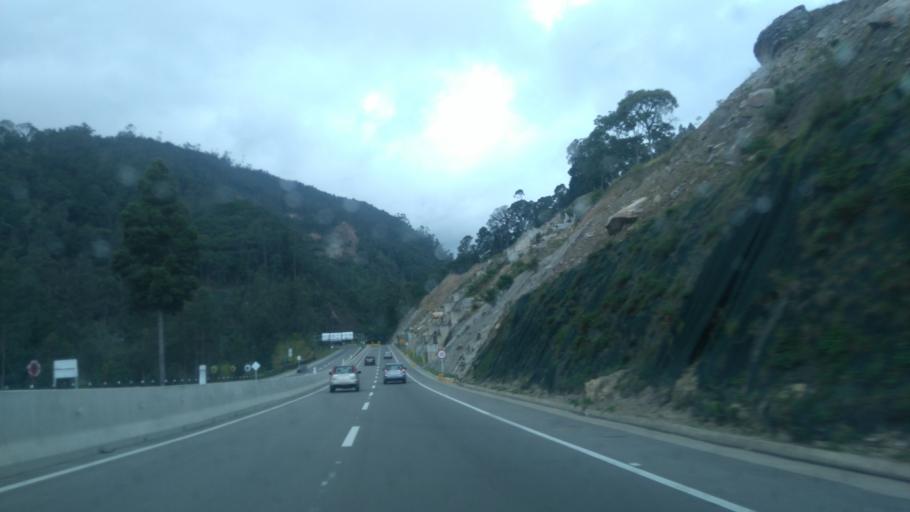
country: CO
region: Cundinamarca
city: El Rosal
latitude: 4.8992
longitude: -74.3113
